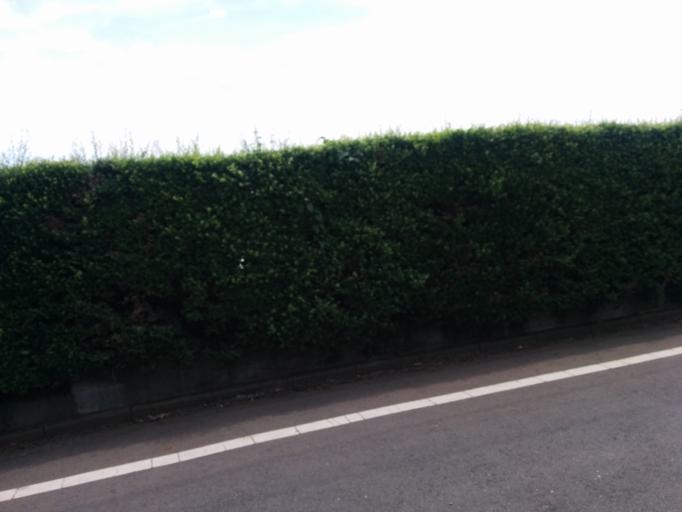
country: JP
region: Tokyo
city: Higashimurayama-shi
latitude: 35.7573
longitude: 139.4837
